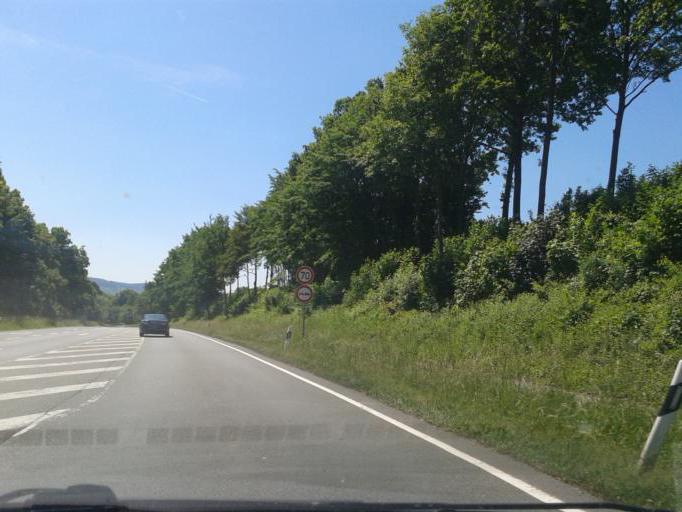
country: DE
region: North Rhine-Westphalia
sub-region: Regierungsbezirk Detmold
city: Blomberg
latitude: 51.9379
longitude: 9.0818
